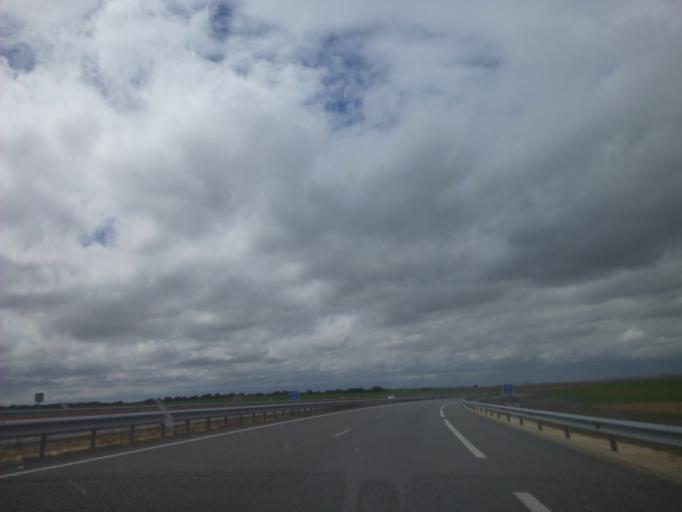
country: ES
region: Castille and Leon
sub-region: Provincia de Salamanca
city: Pelabravo
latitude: 40.9294
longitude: -5.5843
